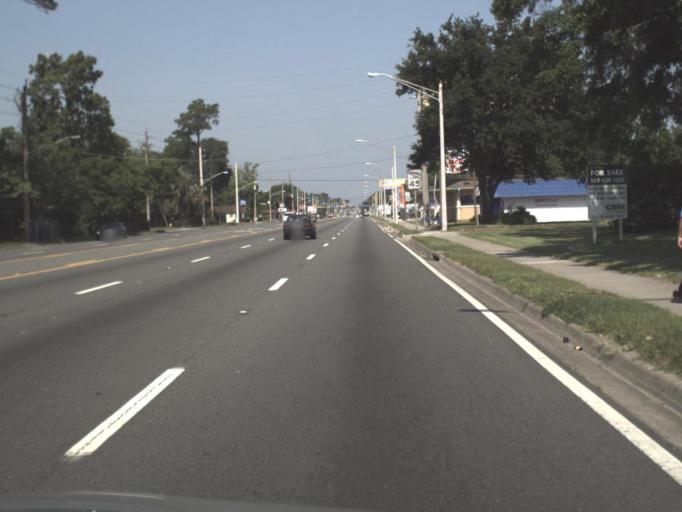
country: US
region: Florida
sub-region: Clay County
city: Bellair-Meadowbrook Terrace
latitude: 30.2485
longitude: -81.7485
